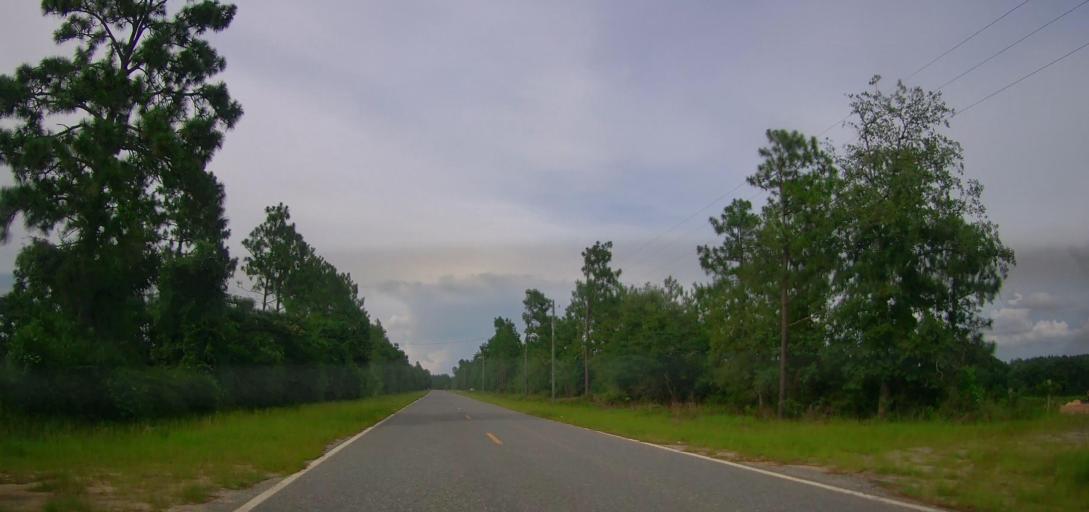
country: US
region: Georgia
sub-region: Wayne County
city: Jesup
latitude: 31.6661
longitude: -81.9124
